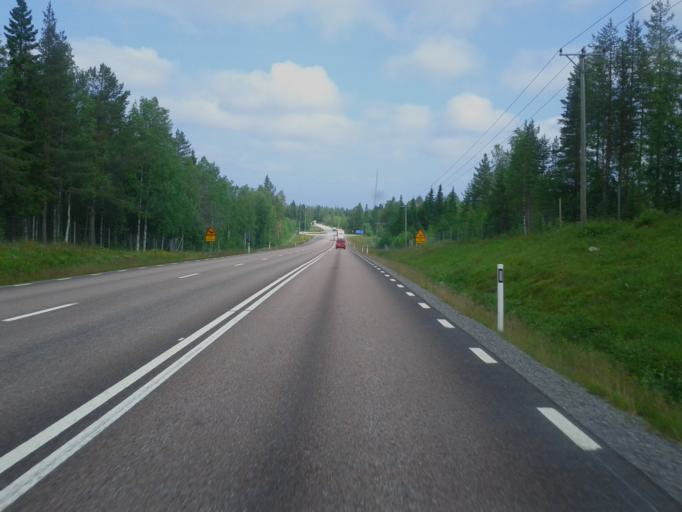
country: SE
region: Vaesterbotten
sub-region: Skelleftea Kommun
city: Burea
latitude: 64.4617
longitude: 21.2912
